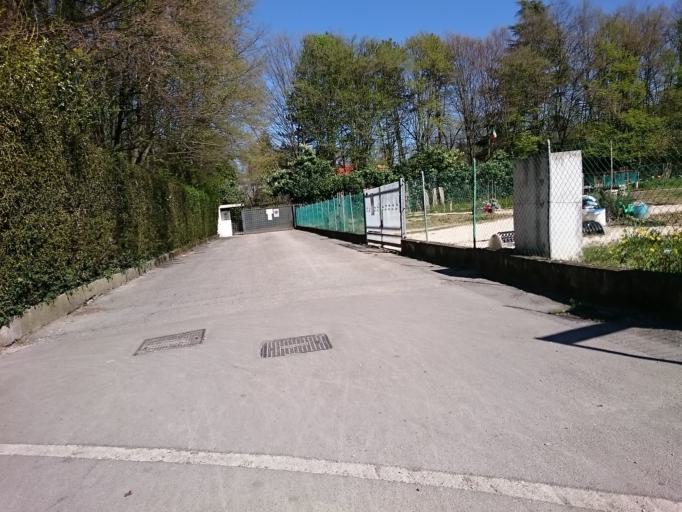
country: IT
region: Veneto
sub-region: Provincia di Padova
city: Padova
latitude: 45.3996
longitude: 11.8994
